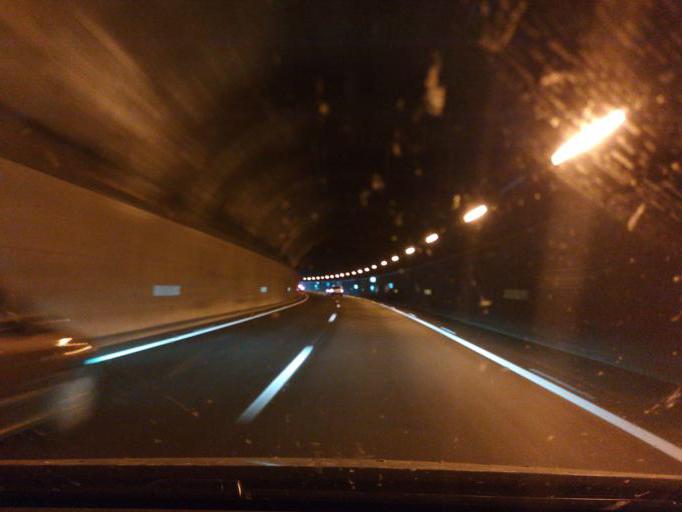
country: ES
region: Valencia
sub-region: Provincia de Valencia
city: Xeresa
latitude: 39.0009
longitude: -0.2256
